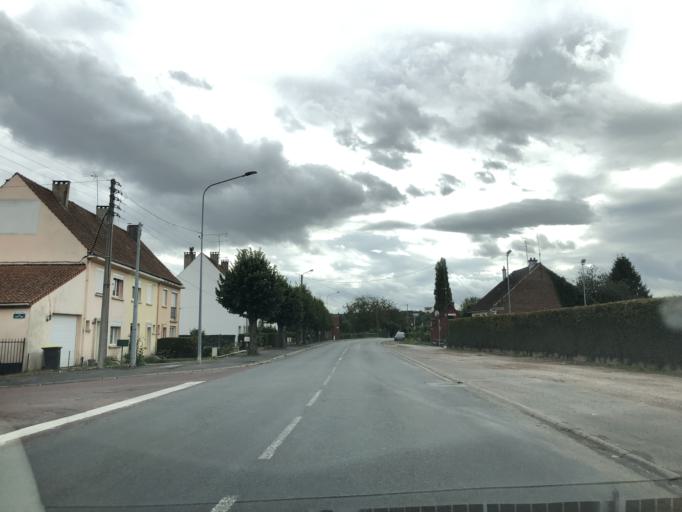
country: FR
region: Nord-Pas-de-Calais
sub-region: Departement du Pas-de-Calais
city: Hesdin
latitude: 50.3758
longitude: 2.0309
